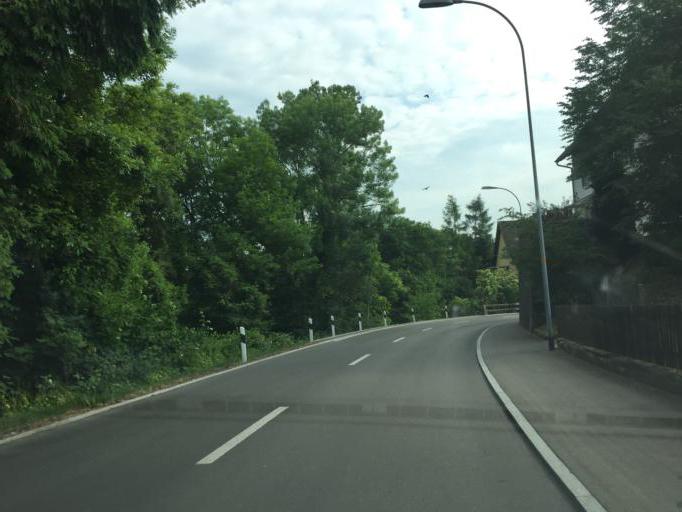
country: CH
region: Zurich
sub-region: Bezirk Andelfingen
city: Dachsen
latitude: 47.6442
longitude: 8.6015
